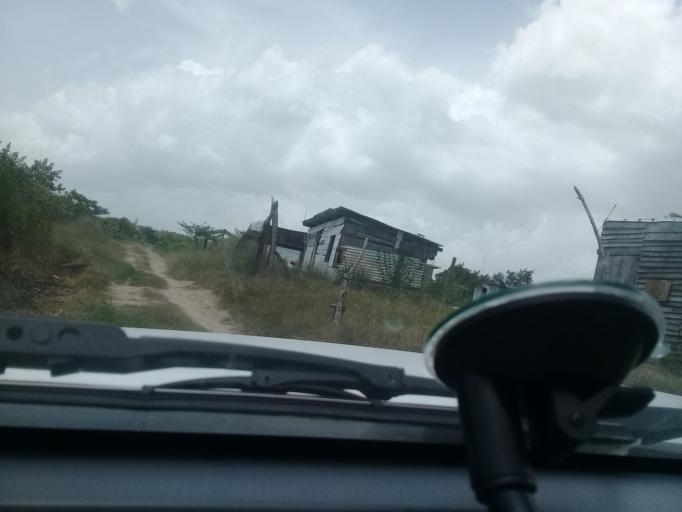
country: MX
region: Veracruz
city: Anahuac
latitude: 22.2247
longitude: -97.8261
